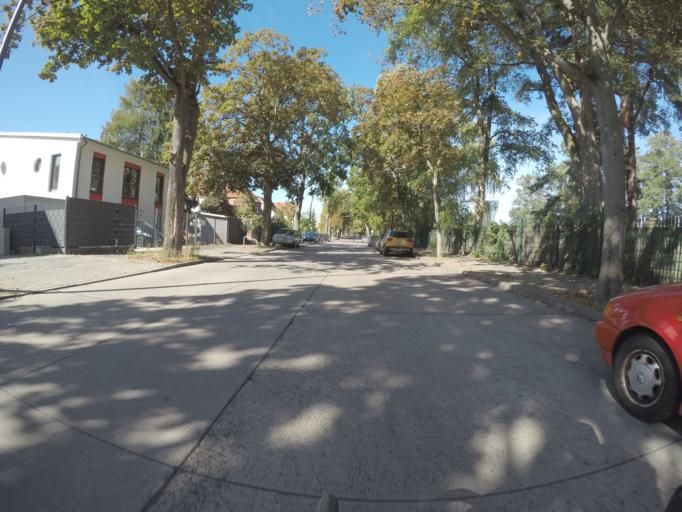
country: DE
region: Berlin
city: Konradshohe
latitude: 52.6004
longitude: 13.2122
